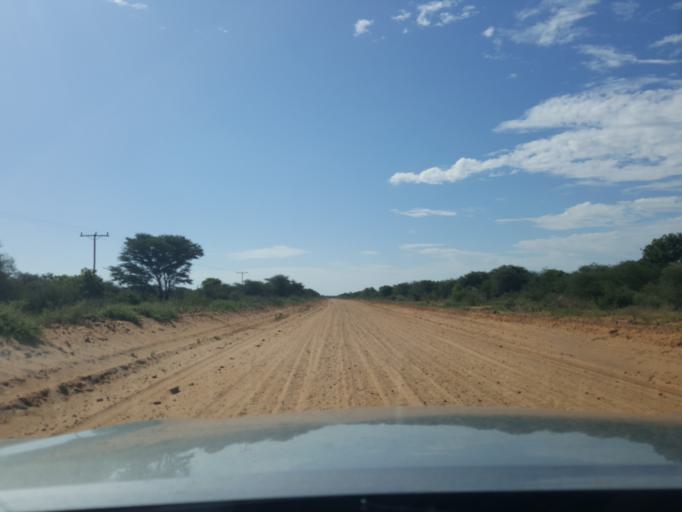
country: BW
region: Kweneng
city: Khudumelapye
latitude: -23.7149
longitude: 24.7324
